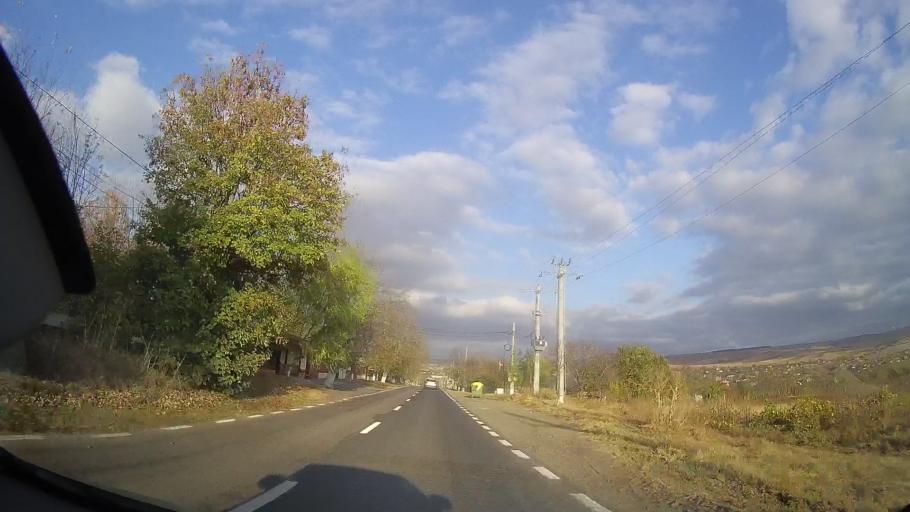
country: RO
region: Tulcea
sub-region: Comuna Topolog
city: Topolog
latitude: 44.8706
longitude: 28.3663
